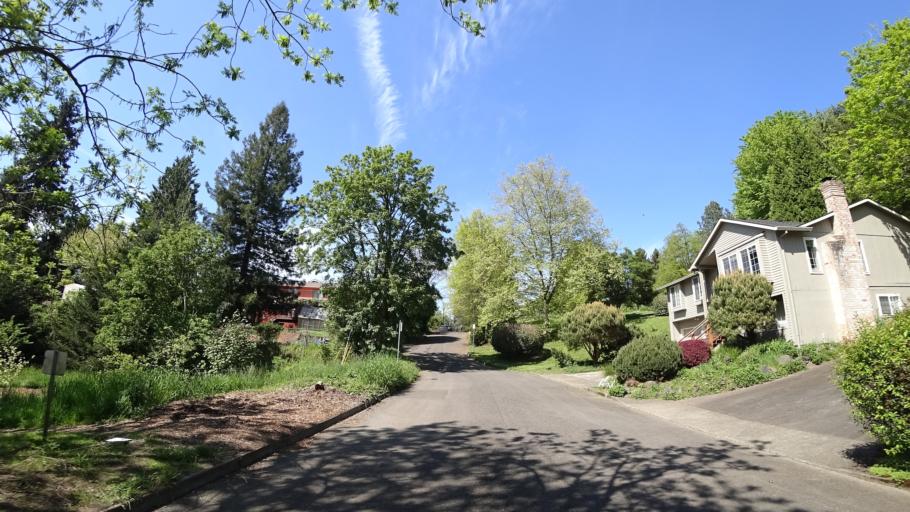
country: US
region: Oregon
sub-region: Clackamas County
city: Milwaukie
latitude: 45.4826
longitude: -122.6247
